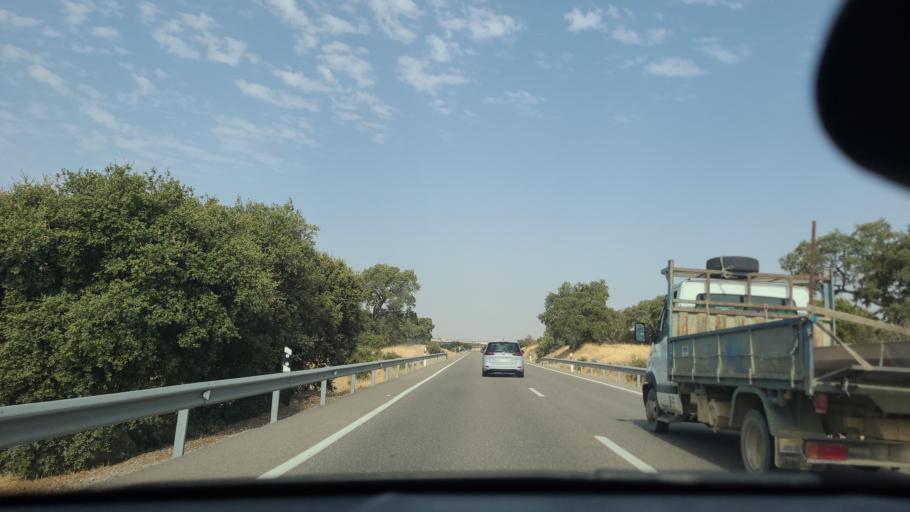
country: ES
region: Andalusia
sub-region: Province of Cordoba
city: Fuente Obejuna
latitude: 38.2619
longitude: -5.4854
